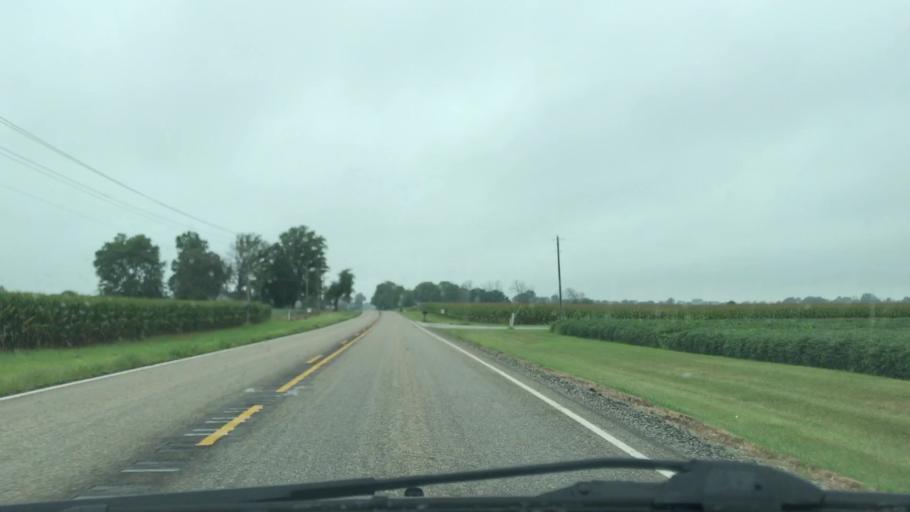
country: US
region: Indiana
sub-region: Boone County
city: Dale
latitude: 40.1277
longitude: -86.3453
